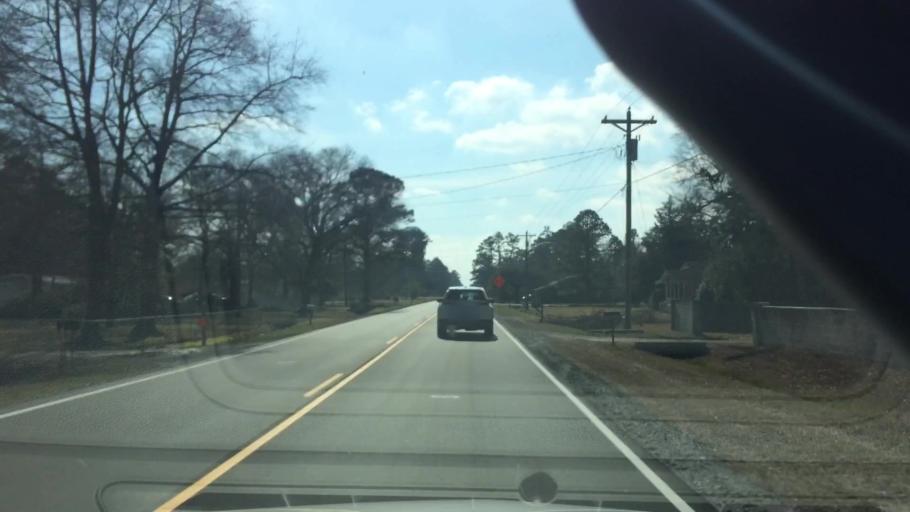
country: US
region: North Carolina
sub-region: Duplin County
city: Beulaville
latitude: 34.9821
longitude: -77.7595
